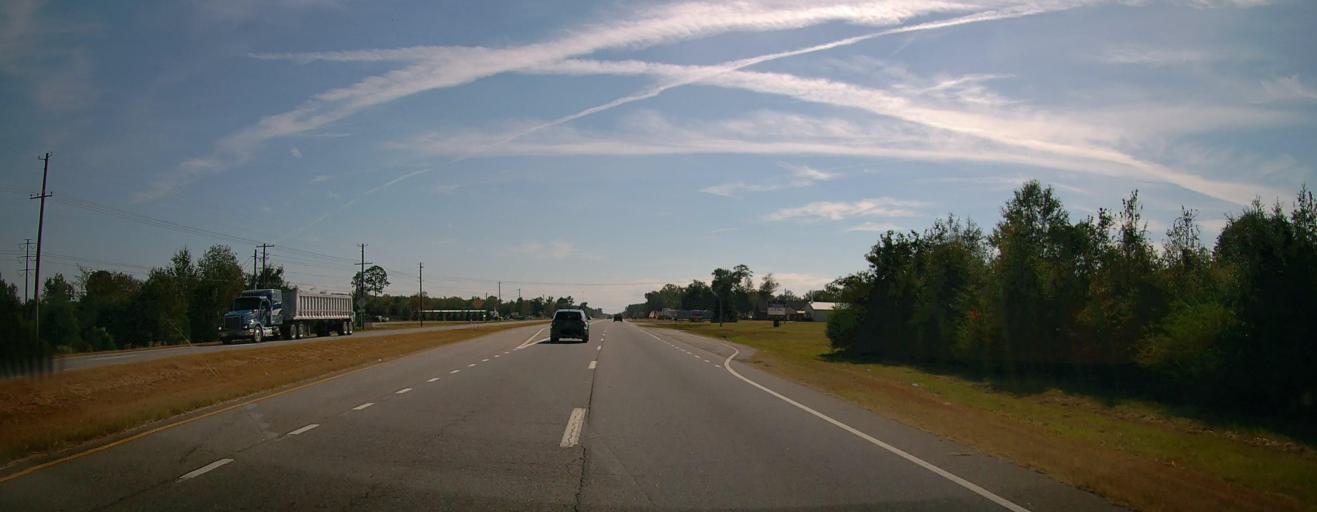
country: US
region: Georgia
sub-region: Dougherty County
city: Putney
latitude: 31.5271
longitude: -84.1157
